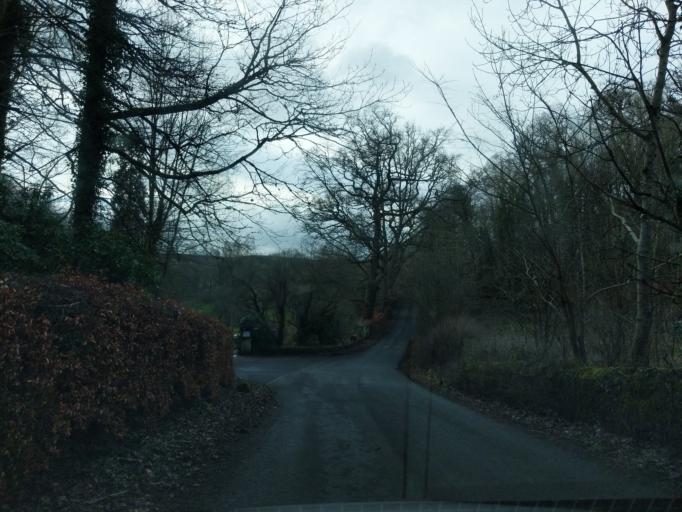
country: GB
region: Scotland
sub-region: South Lanarkshire
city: Carluke
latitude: 55.7063
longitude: -3.8607
